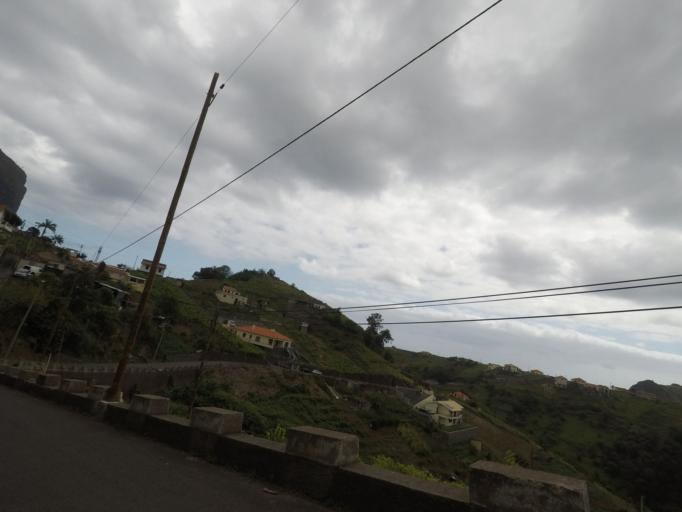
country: PT
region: Madeira
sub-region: Santana
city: Santana
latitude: 32.7666
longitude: -16.8315
